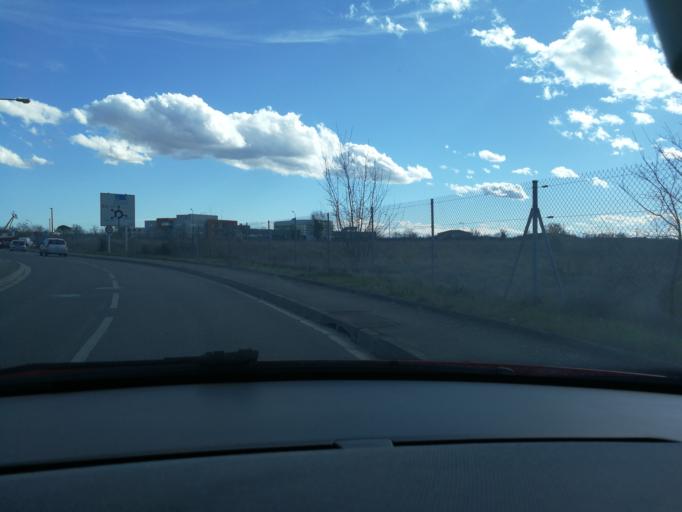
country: FR
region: Midi-Pyrenees
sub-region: Departement de la Haute-Garonne
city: Portet-sur-Garonne
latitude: 43.5468
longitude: 1.3856
